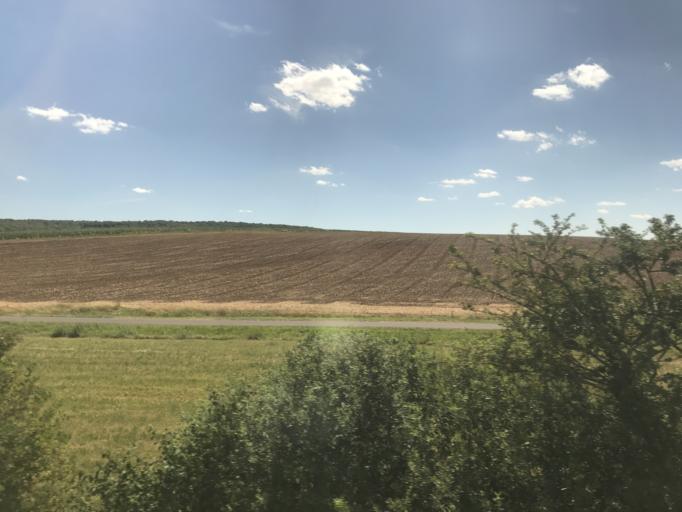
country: FR
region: Lorraine
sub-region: Departement de la Moselle
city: Remilly
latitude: 48.9630
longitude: 6.4859
